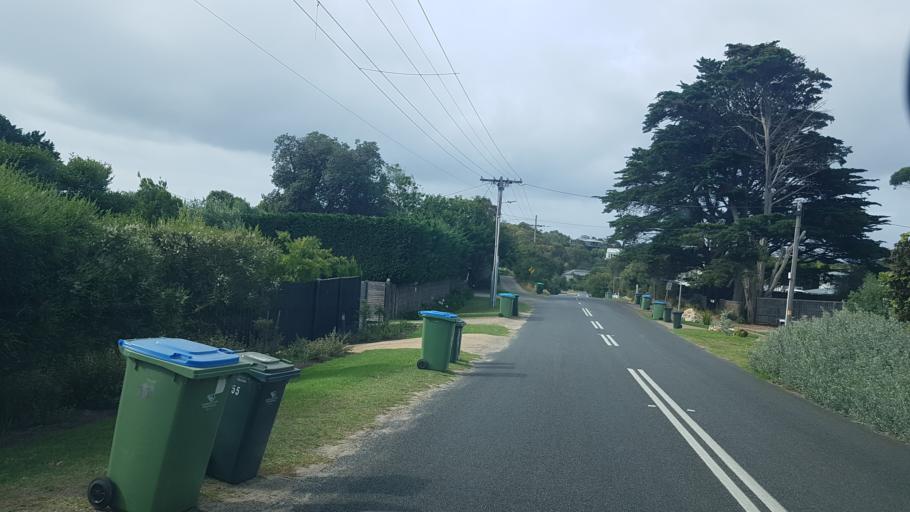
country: AU
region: Victoria
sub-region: Mornington Peninsula
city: Sorrento
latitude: -38.3248
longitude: 144.7111
